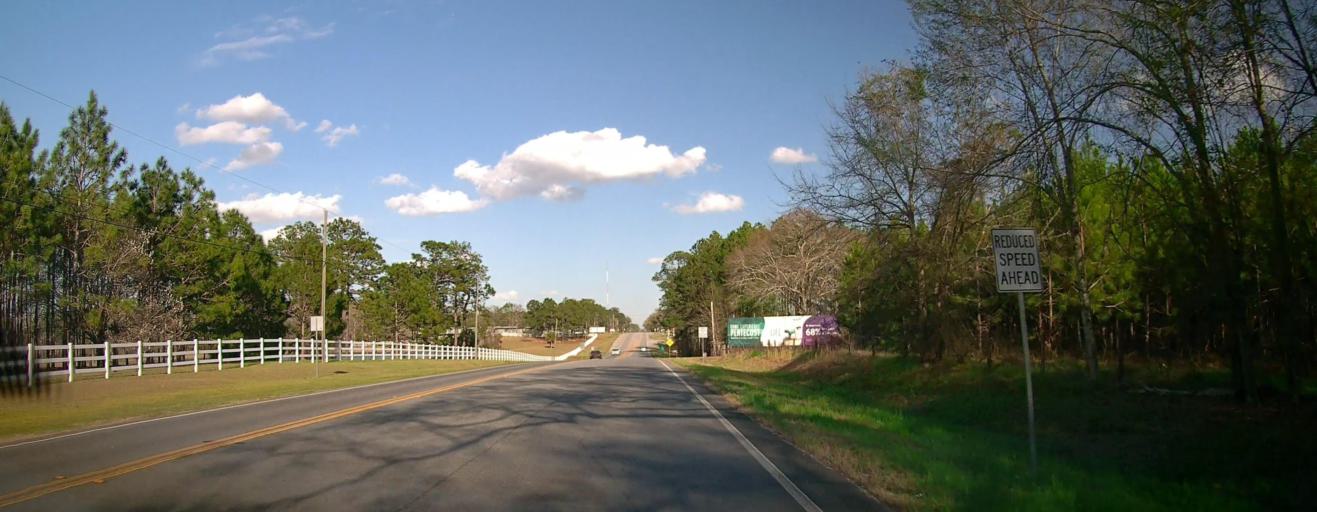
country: US
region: Georgia
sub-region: Toombs County
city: Vidalia
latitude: 32.2171
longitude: -82.4474
